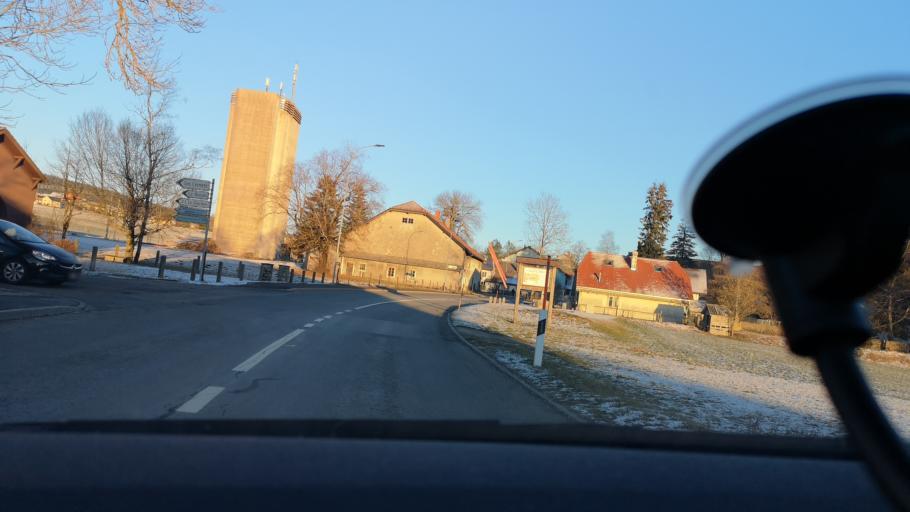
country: CH
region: Vaud
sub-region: Jura-Nord vaudois District
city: Sainte-Croix
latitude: 46.9036
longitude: 6.4753
